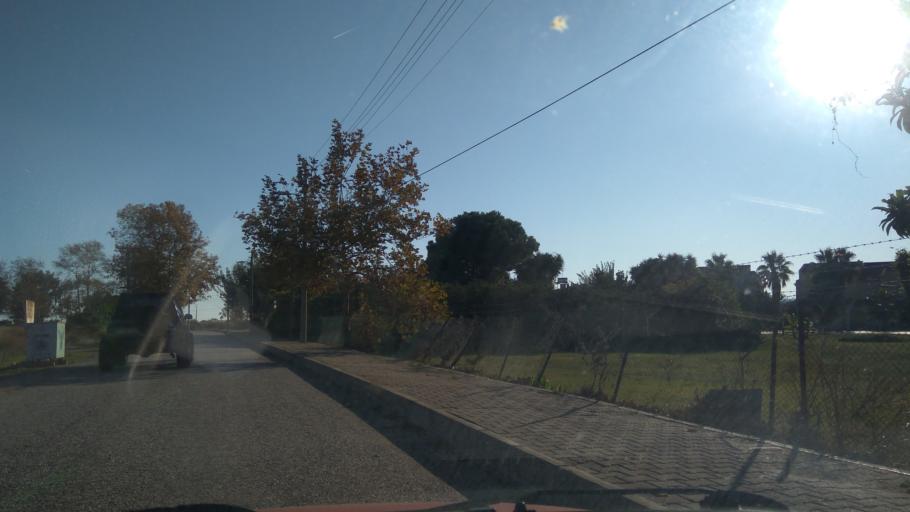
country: TR
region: Antalya
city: Kemer
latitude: 36.5633
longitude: 30.5714
